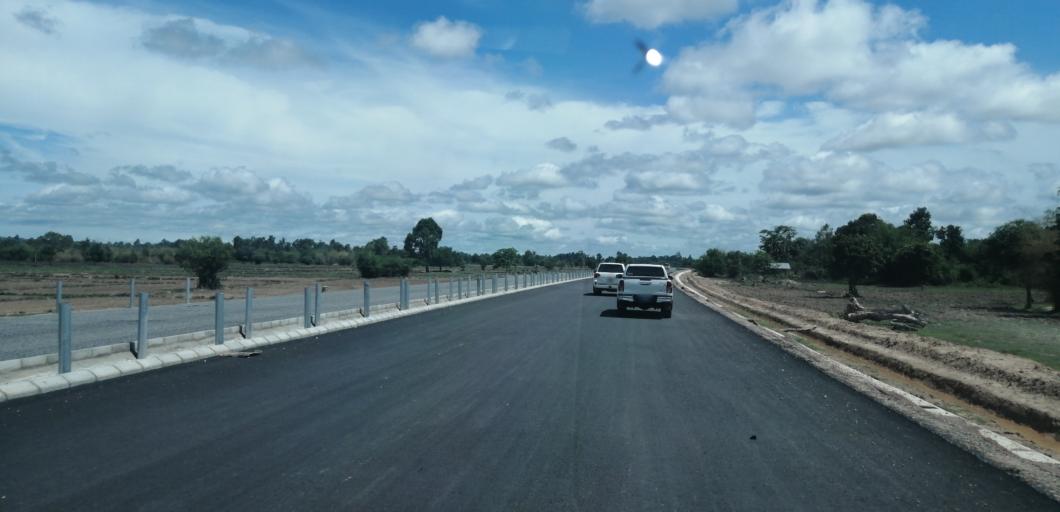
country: LA
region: Vientiane
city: Vientiane
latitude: 18.0680
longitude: 102.5164
